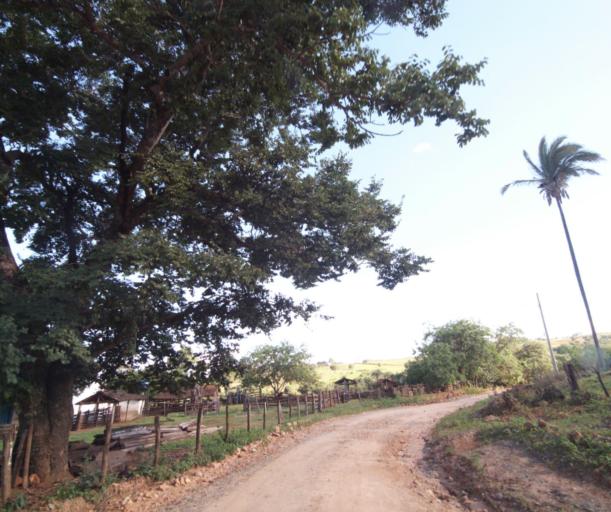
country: BR
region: Bahia
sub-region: Carinhanha
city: Carinhanha
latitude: -14.2626
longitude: -44.5251
